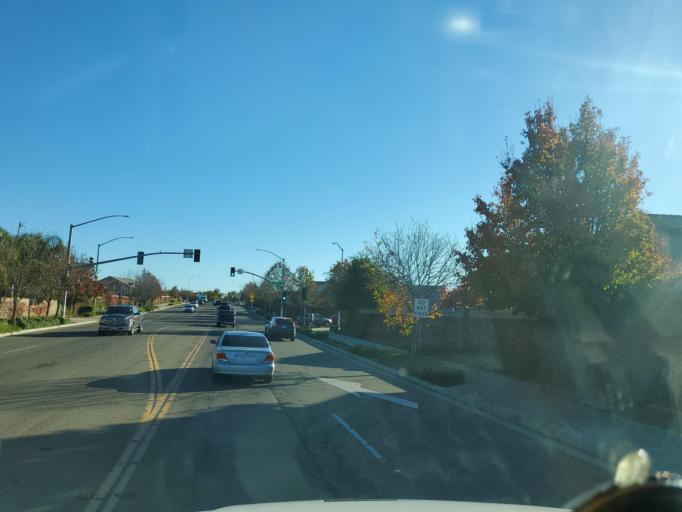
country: US
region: California
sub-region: San Joaquin County
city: August
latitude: 38.0023
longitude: -121.2713
